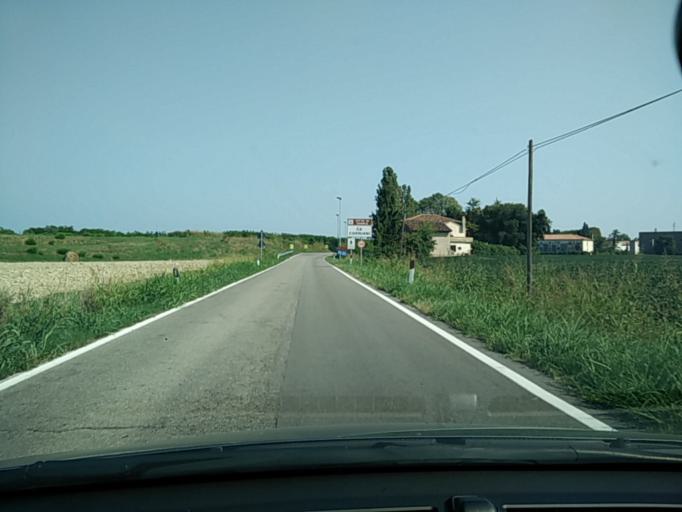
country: IT
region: Veneto
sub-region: Provincia di Venezia
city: Caorle
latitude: 45.6172
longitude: 12.8583
